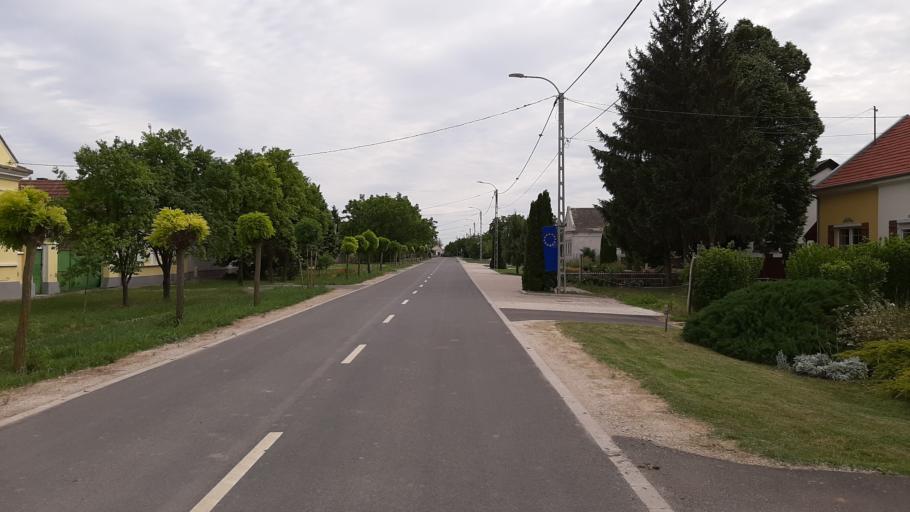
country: RO
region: Timis
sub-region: Comuna Beba Veche
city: Beba Veche
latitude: 46.1470
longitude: 20.2752
